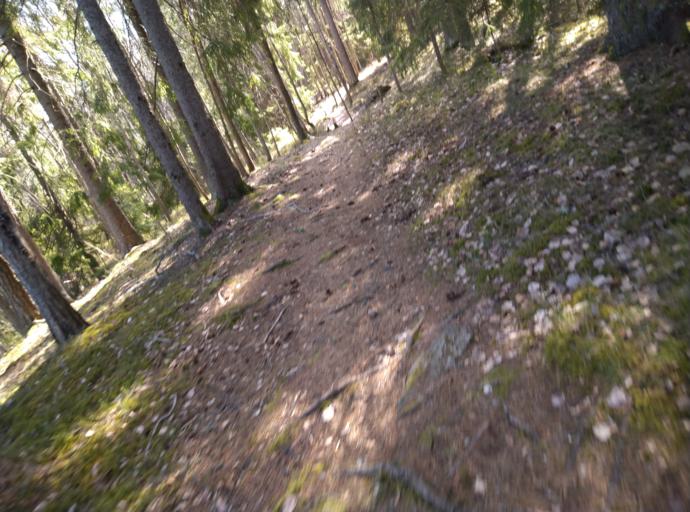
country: SE
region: Stockholm
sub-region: Nacka Kommun
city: Fisksatra
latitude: 59.2956
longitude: 18.2477
